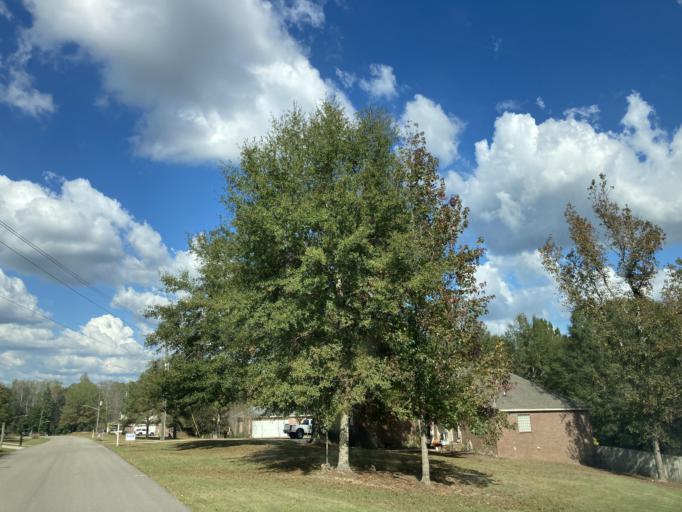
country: US
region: Mississippi
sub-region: Lamar County
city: Sumrall
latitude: 31.3970
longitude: -89.5391
